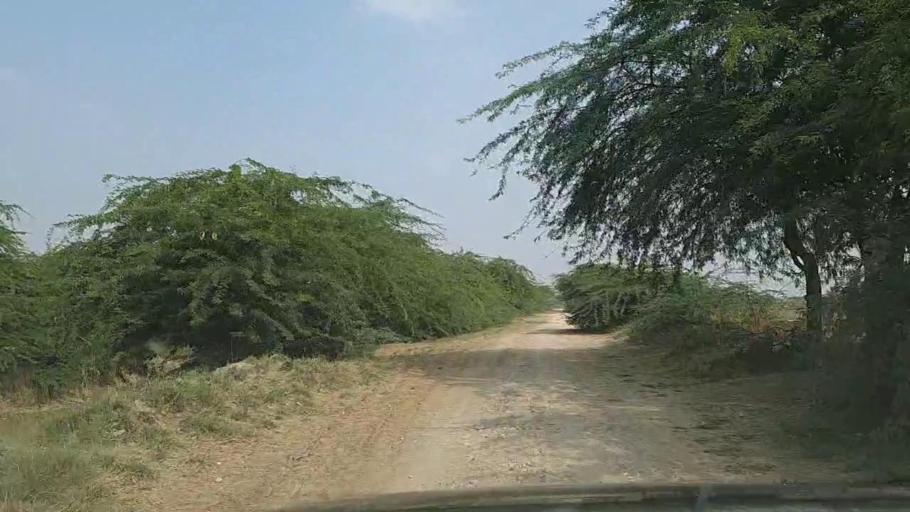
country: PK
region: Sindh
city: Thatta
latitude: 24.7756
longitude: 67.8312
